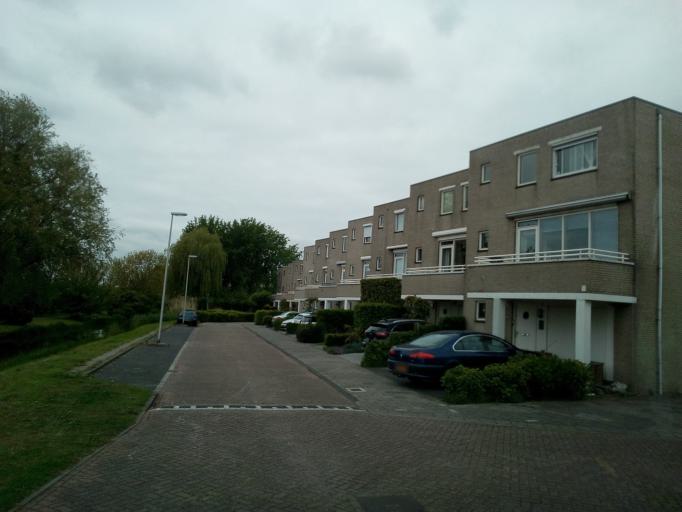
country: NL
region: South Holland
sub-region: Gemeente Alphen aan den Rijn
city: Alphen aan den Rijn
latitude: 52.1190
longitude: 4.6642
